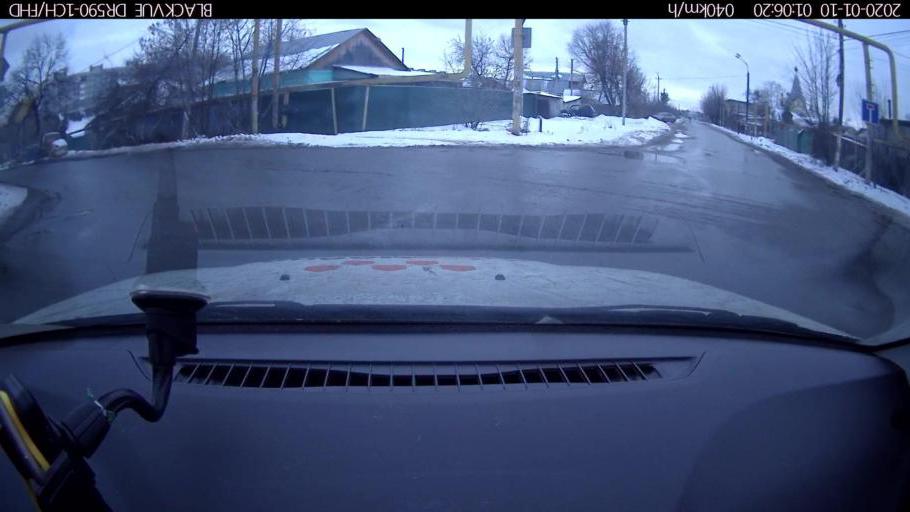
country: RU
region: Nizjnij Novgorod
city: Nizhniy Novgorod
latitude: 56.2771
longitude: 43.8848
